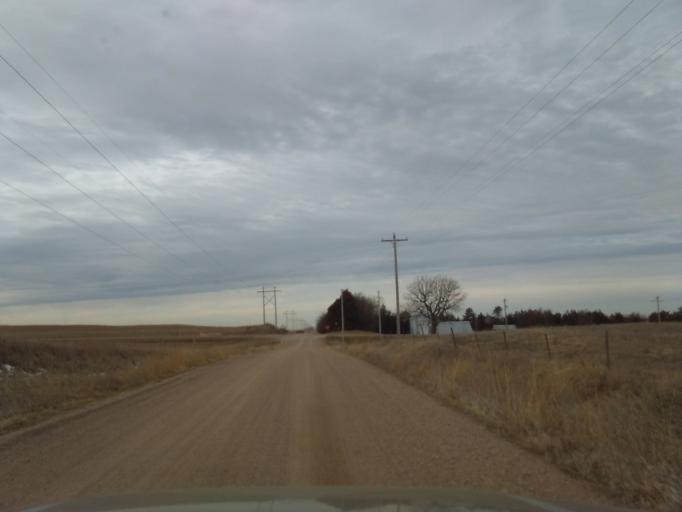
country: US
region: Nebraska
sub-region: Buffalo County
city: Shelton
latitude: 40.6548
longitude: -98.7225
